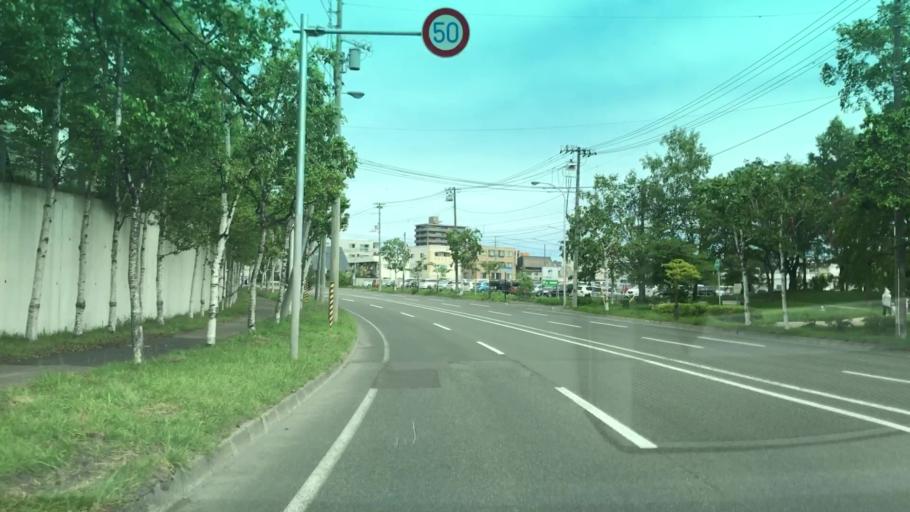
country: JP
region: Hokkaido
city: Sapporo
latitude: 43.0693
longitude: 141.2875
